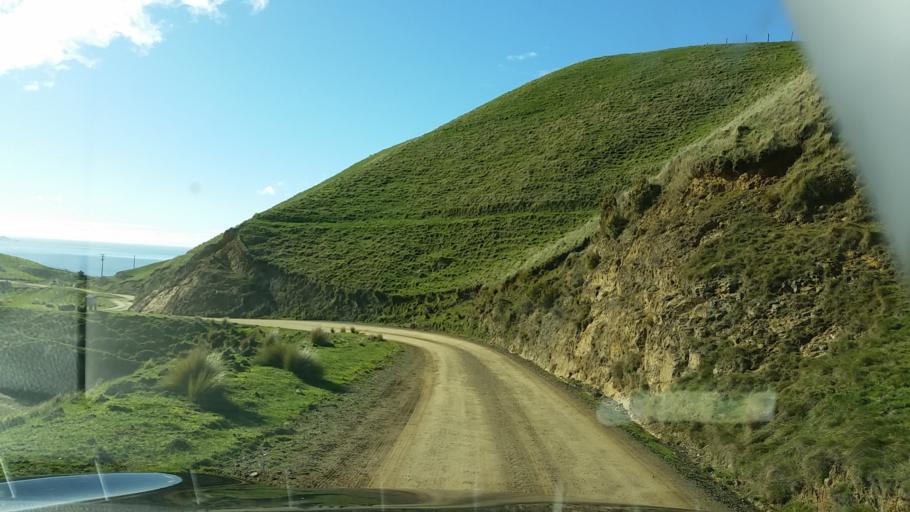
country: NZ
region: Marlborough
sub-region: Marlborough District
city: Picton
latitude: -40.9511
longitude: 173.8339
